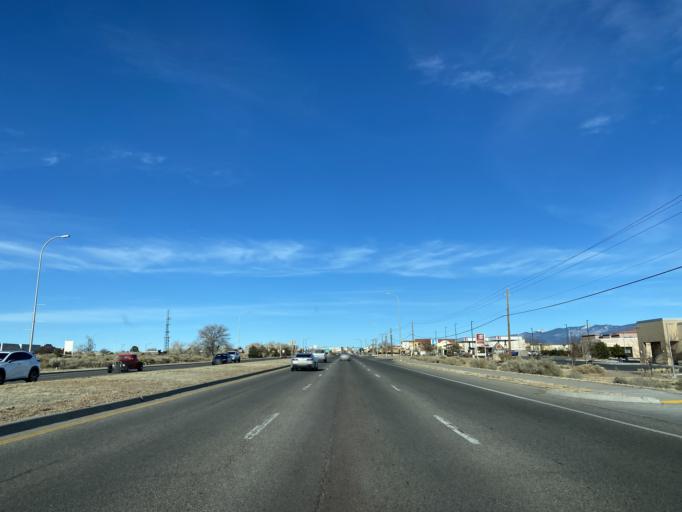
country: US
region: New Mexico
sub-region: Santa Fe County
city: Agua Fria
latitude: 35.6318
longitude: -106.0217
